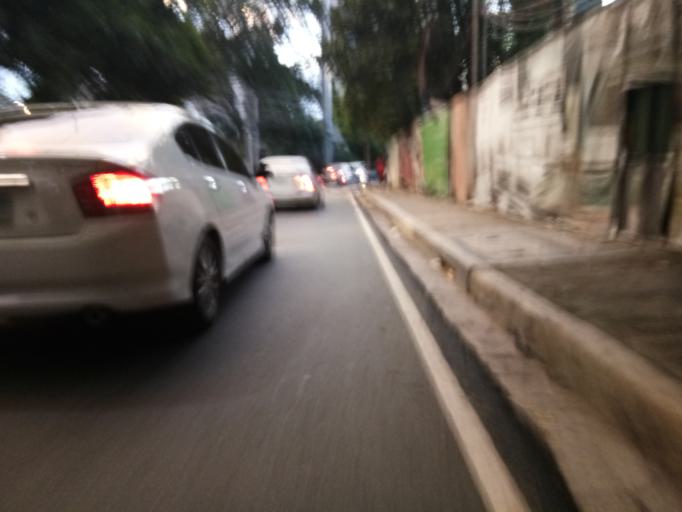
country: PH
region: Metro Manila
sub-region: San Juan
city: San Juan
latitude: 14.6133
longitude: 121.0387
